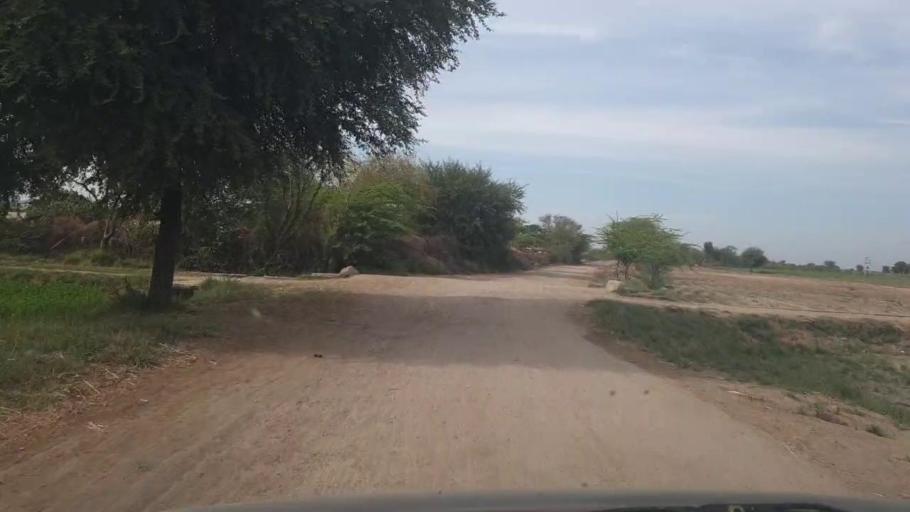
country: PK
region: Sindh
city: Kunri
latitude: 25.2756
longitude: 69.6036
